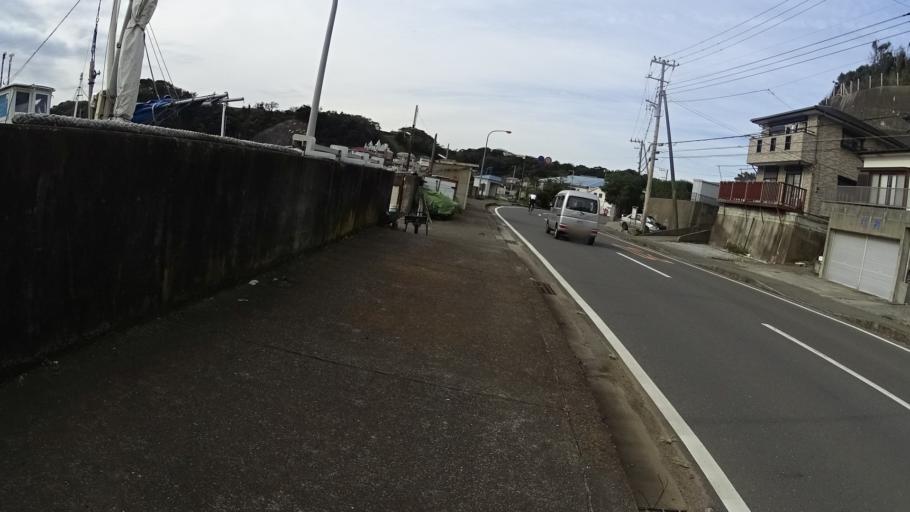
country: JP
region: Kanagawa
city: Miura
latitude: 35.1459
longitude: 139.6680
